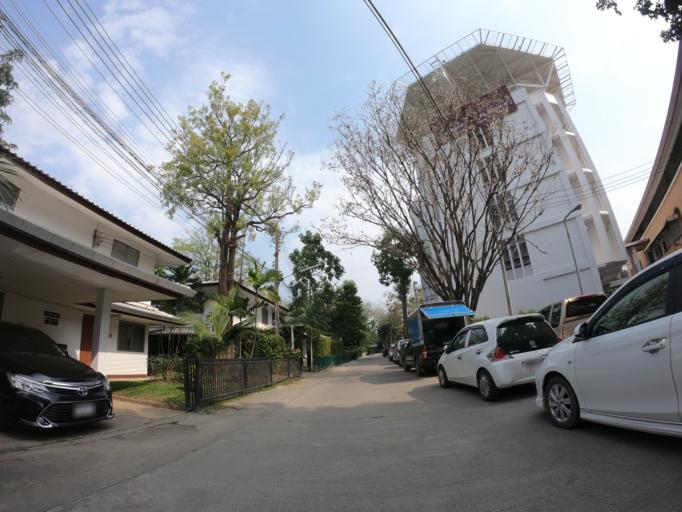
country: TH
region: Chiang Mai
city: Chiang Mai
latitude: 18.7606
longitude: 98.9990
